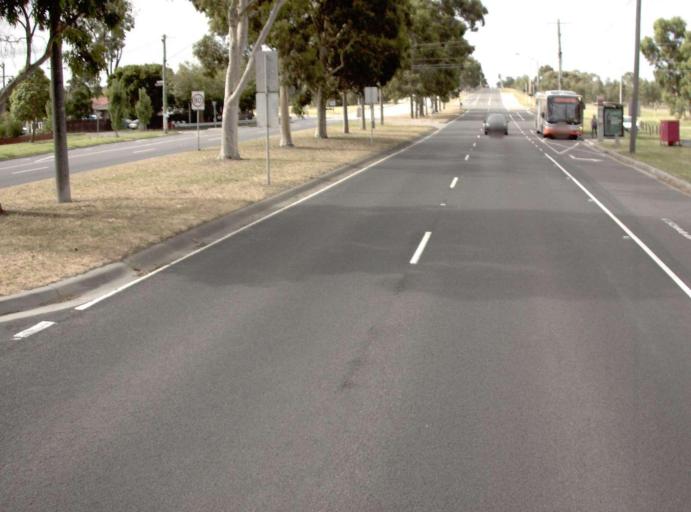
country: AU
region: Victoria
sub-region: Greater Dandenong
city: Dandenong North
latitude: -37.9638
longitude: 145.2248
